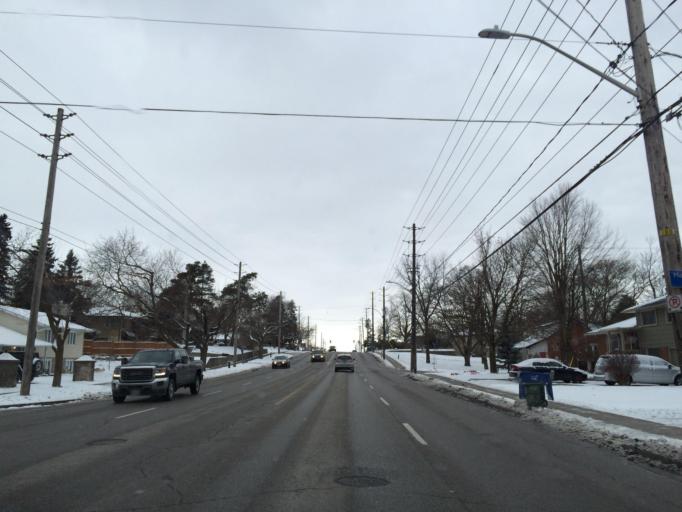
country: CA
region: Ontario
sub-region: Wellington County
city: Guelph
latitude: 43.5277
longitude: -80.2447
